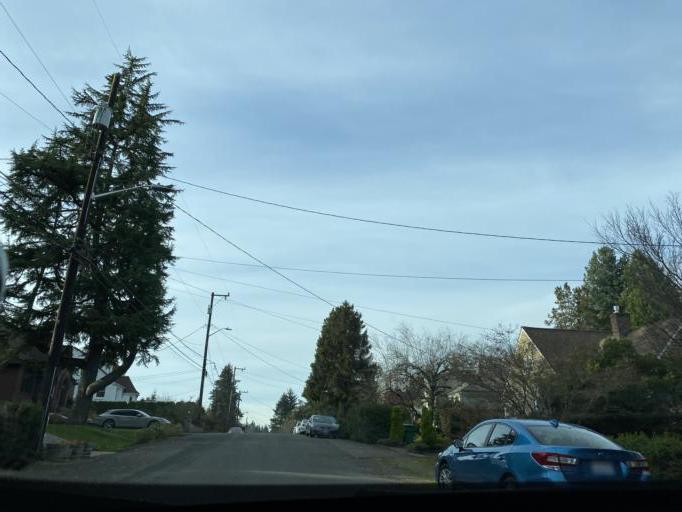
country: US
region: Washington
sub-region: King County
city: Lake Forest Park
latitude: 47.7002
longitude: -122.2939
